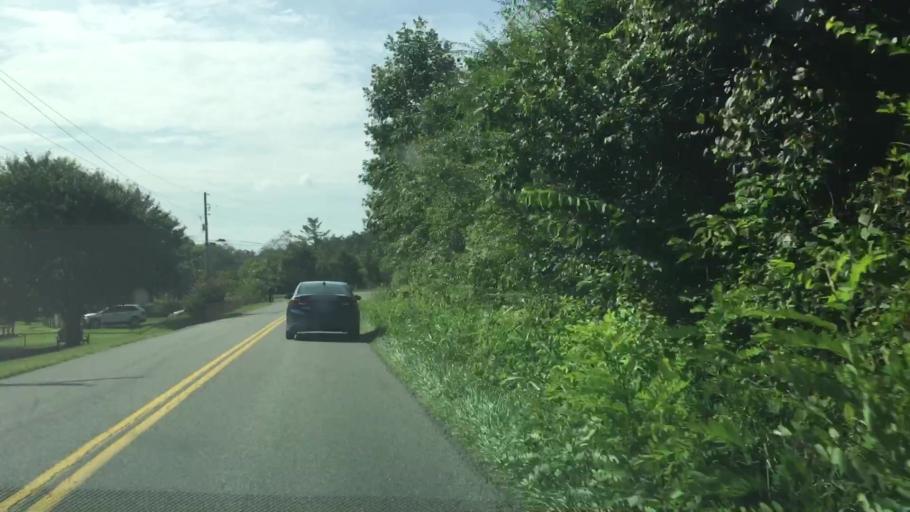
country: US
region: Tennessee
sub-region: Sullivan County
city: Fairmount
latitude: 36.6102
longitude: -82.0761
